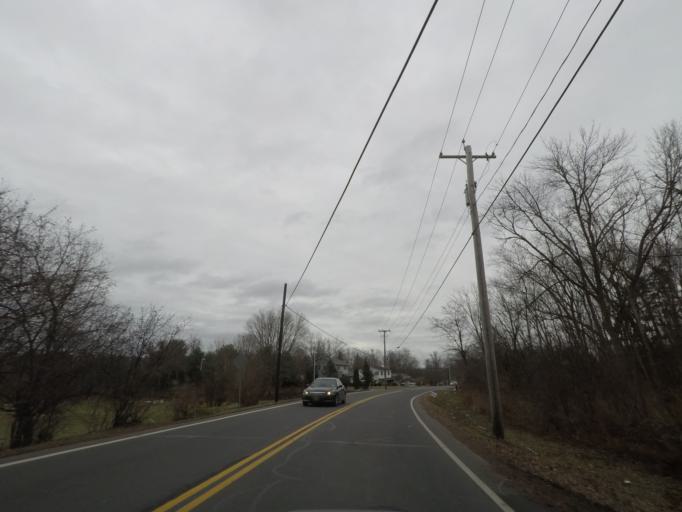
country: US
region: New York
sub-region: Schenectady County
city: Niskayuna
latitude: 42.7749
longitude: -73.8786
